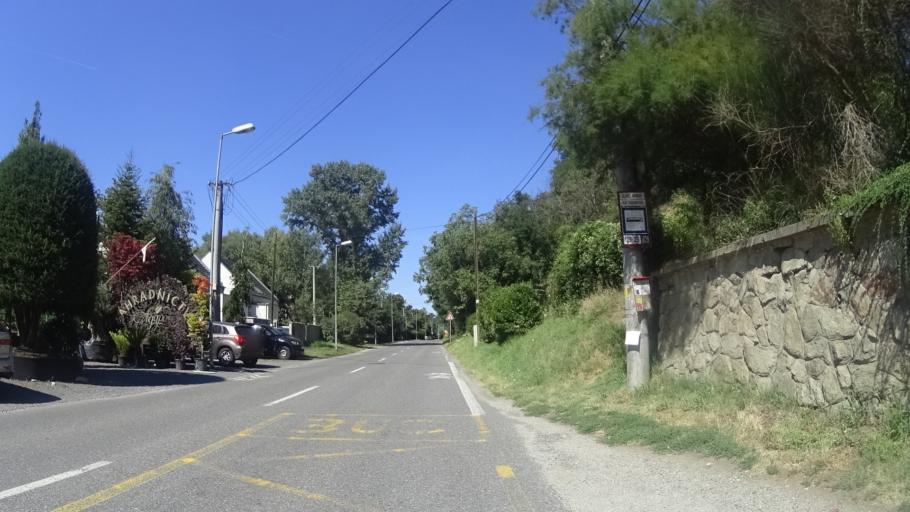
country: AT
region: Lower Austria
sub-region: Politischer Bezirk Bruck an der Leitha
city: Wolfsthal
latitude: 48.1517
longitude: 17.0316
